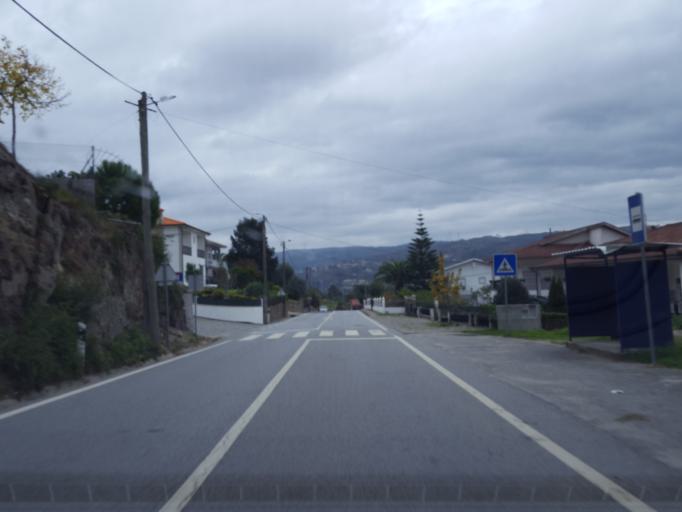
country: PT
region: Porto
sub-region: Marco de Canaveses
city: Marco de Canavezes
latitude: 41.1353
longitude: -8.1326
